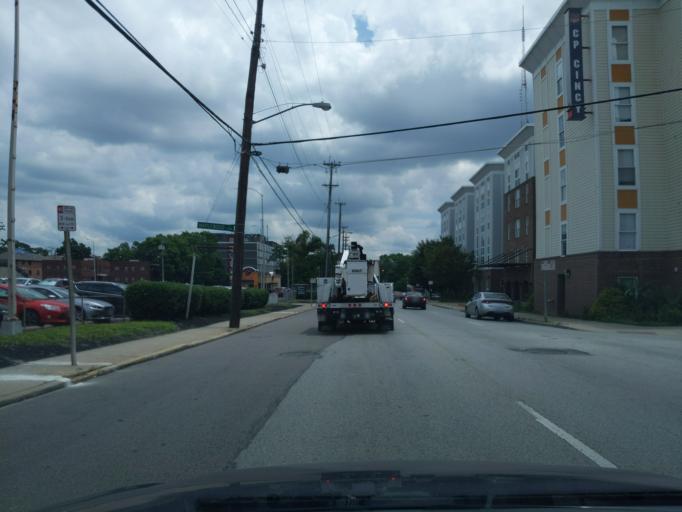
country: US
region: Kentucky
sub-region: Campbell County
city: Bellevue
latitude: 39.1269
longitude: -84.5048
